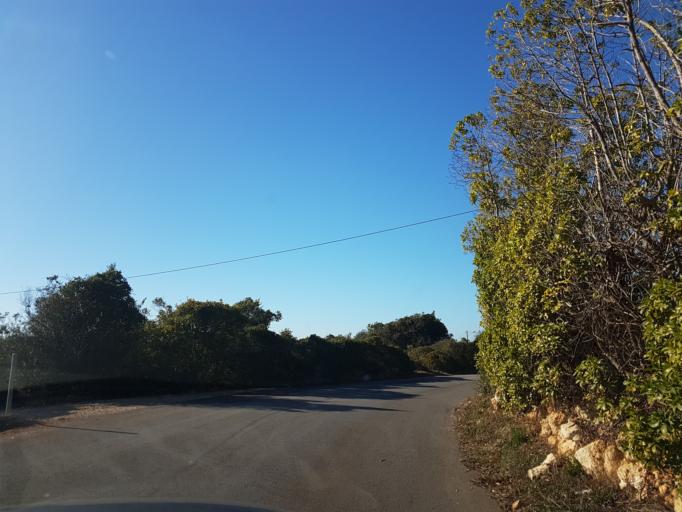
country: PT
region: Faro
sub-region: Lagoa
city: Carvoeiro
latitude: 37.0923
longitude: -8.4192
